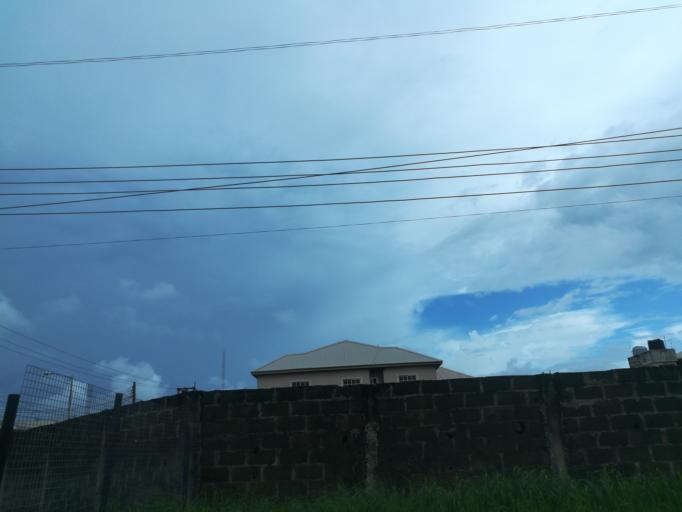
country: NG
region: Lagos
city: Ikoyi
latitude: 6.4425
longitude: 3.4799
